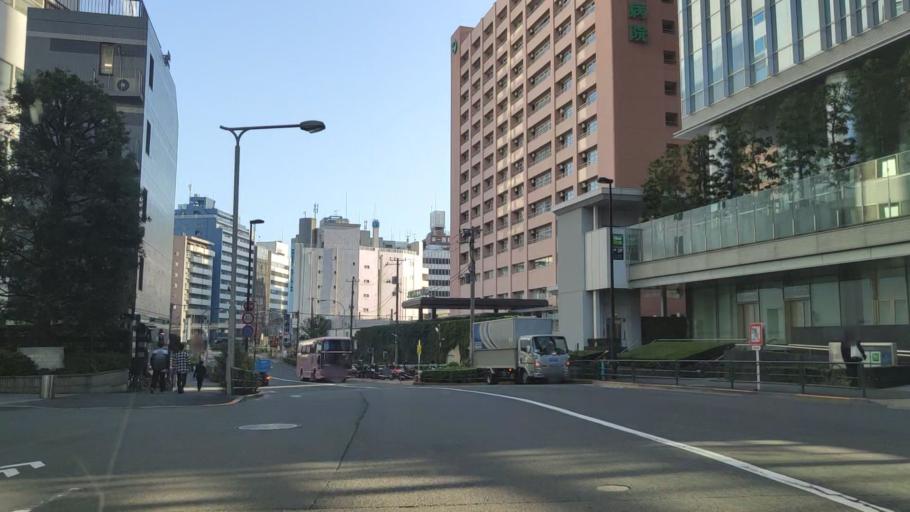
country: JP
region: Tokyo
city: Tokyo
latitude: 35.6868
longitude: 139.6996
